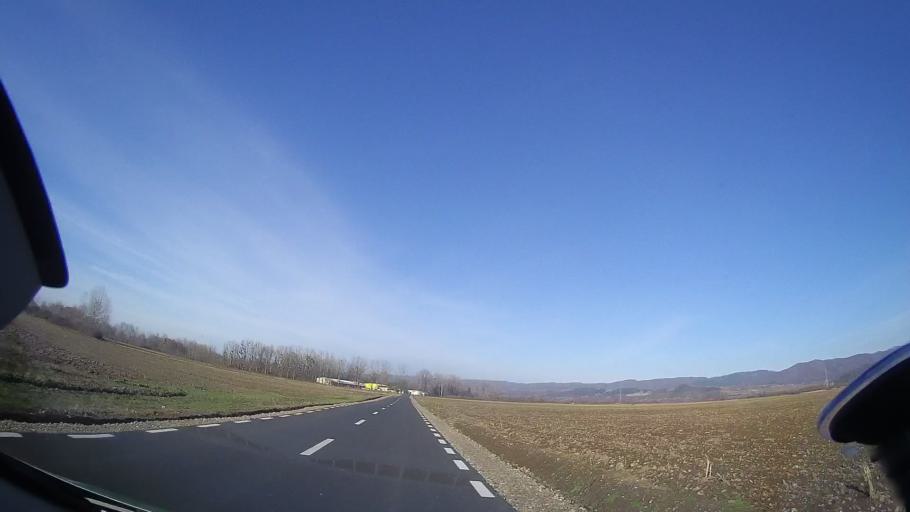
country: RO
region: Bihor
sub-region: Comuna Vadu Crisului
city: Vadu Crisului
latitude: 47.0005
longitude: 22.5037
